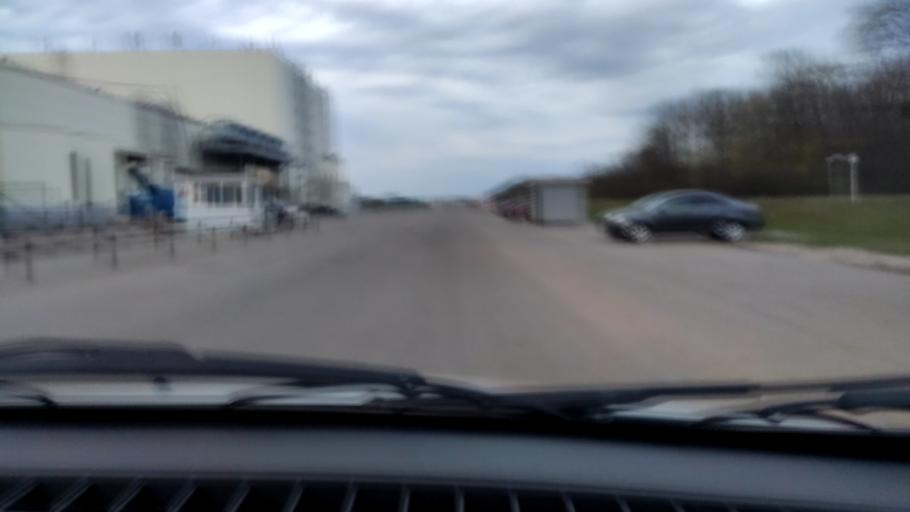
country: RU
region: Voronezj
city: Podgornoye
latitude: 51.7869
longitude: 39.2057
